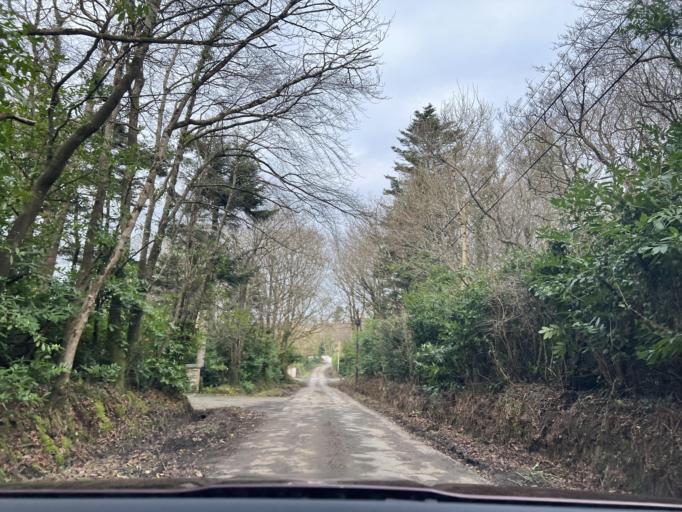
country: IE
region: Leinster
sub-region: Loch Garman
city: Loch Garman
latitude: 52.3672
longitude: -6.5331
